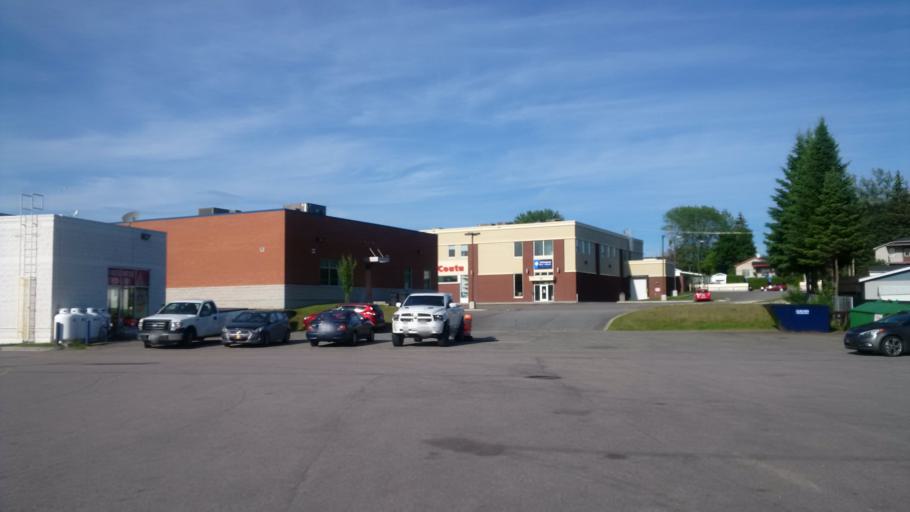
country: CA
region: Quebec
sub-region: Laurentides
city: Mont-Laurier
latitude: 46.5502
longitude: -75.4885
